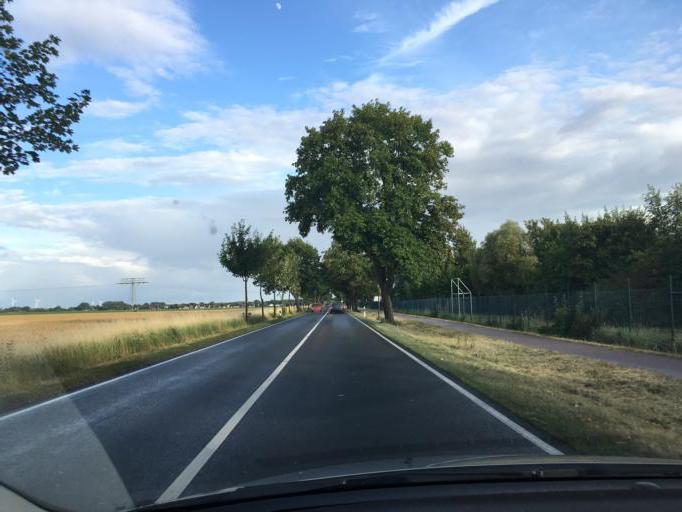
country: DE
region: Saxony-Anhalt
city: Weissandt-Golzau
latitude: 51.6708
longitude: 12.0852
